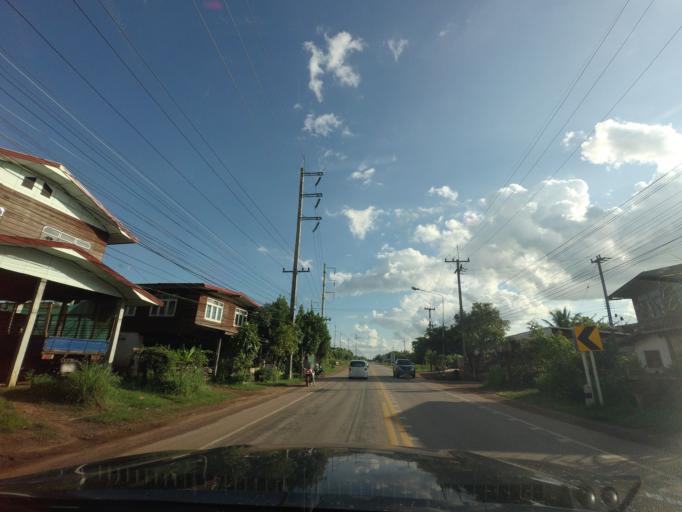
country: TH
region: Changwat Udon Thani
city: Thung Fon
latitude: 17.4877
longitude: 103.1969
